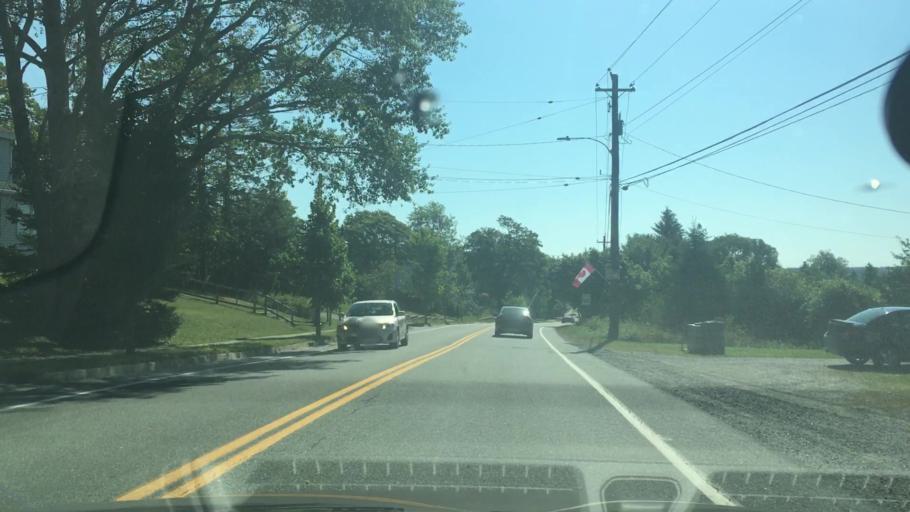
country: CA
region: Nova Scotia
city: New Glasgow
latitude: 44.9274
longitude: -62.5433
